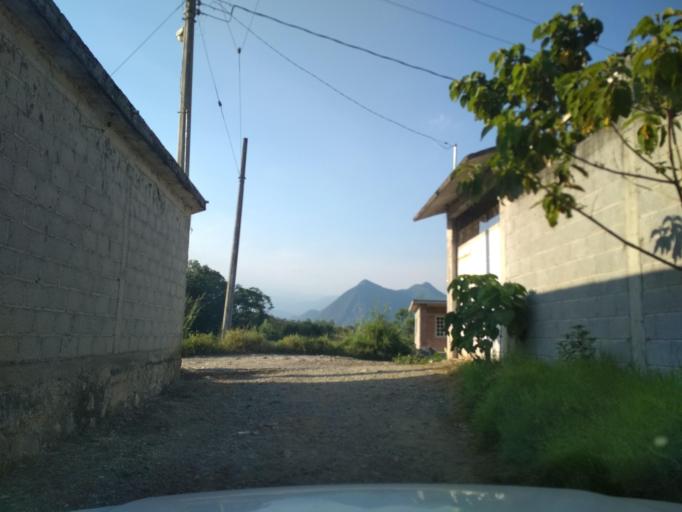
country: MX
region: Veracruz
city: Jalapilla
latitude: 18.8204
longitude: -97.0718
